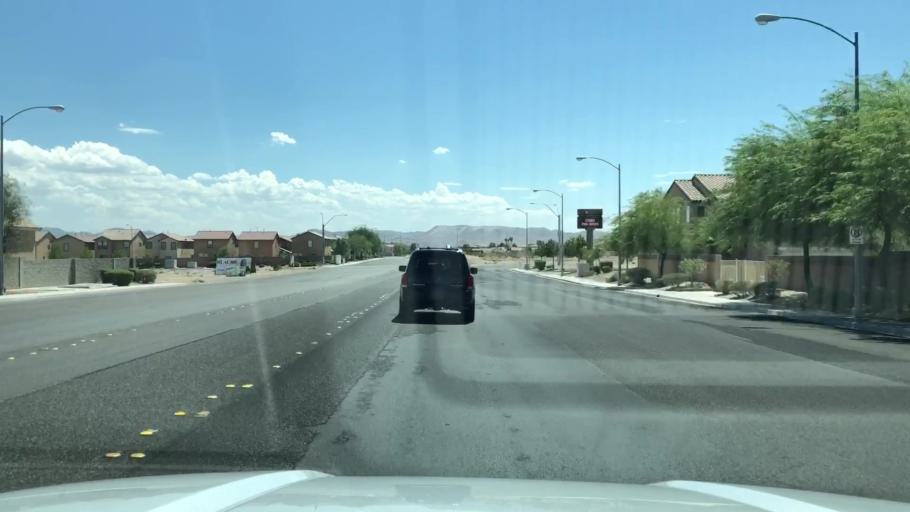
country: US
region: Nevada
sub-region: Clark County
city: Enterprise
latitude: 36.0433
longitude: -115.2083
